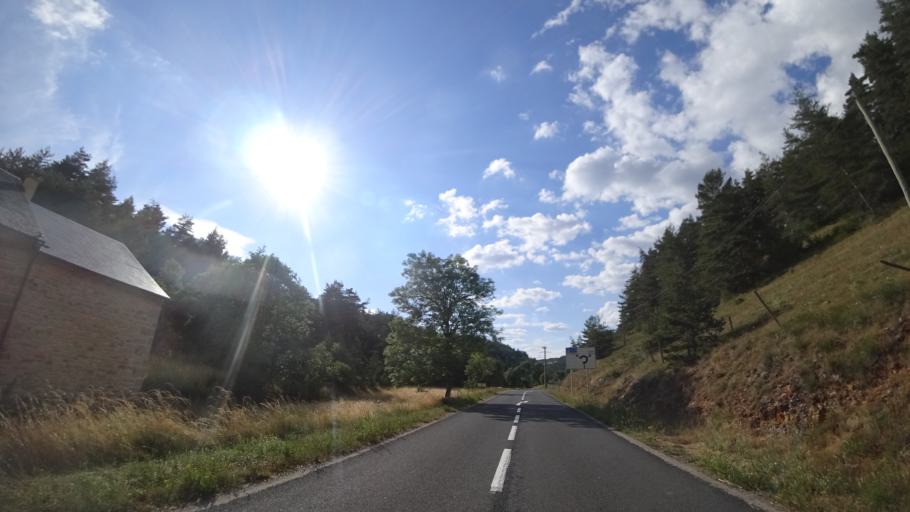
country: FR
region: Languedoc-Roussillon
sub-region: Departement de la Lozere
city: La Canourgue
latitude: 44.4016
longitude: 3.2920
